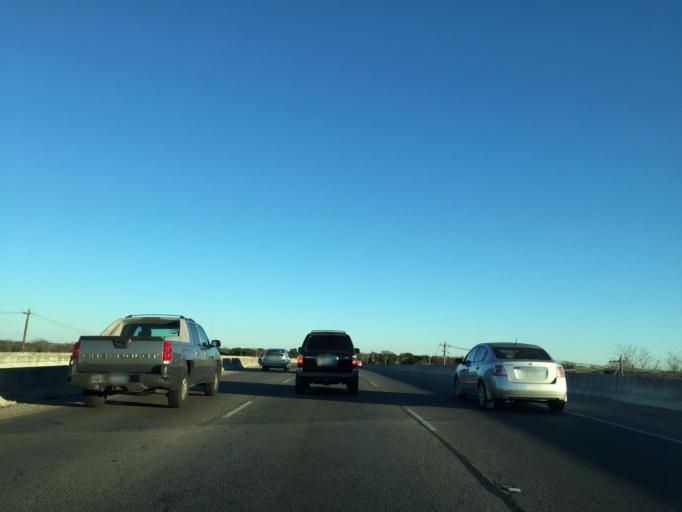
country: US
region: Texas
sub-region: Williamson County
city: Jollyville
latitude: 30.4328
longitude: -97.7296
